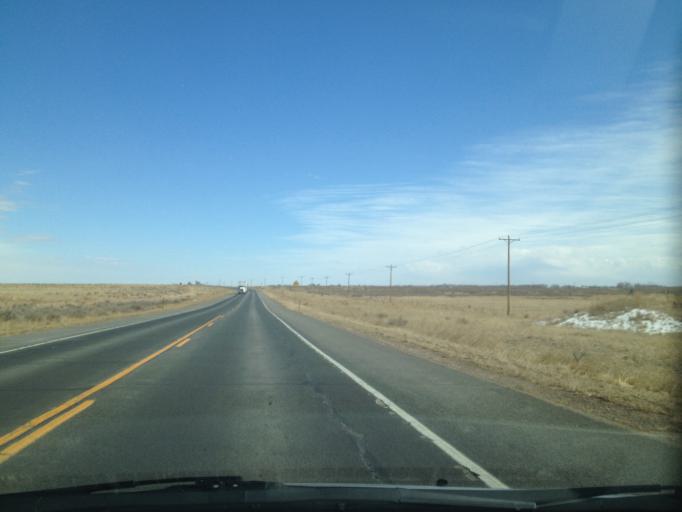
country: US
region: Colorado
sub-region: Weld County
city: Kersey
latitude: 40.2918
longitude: -104.2772
